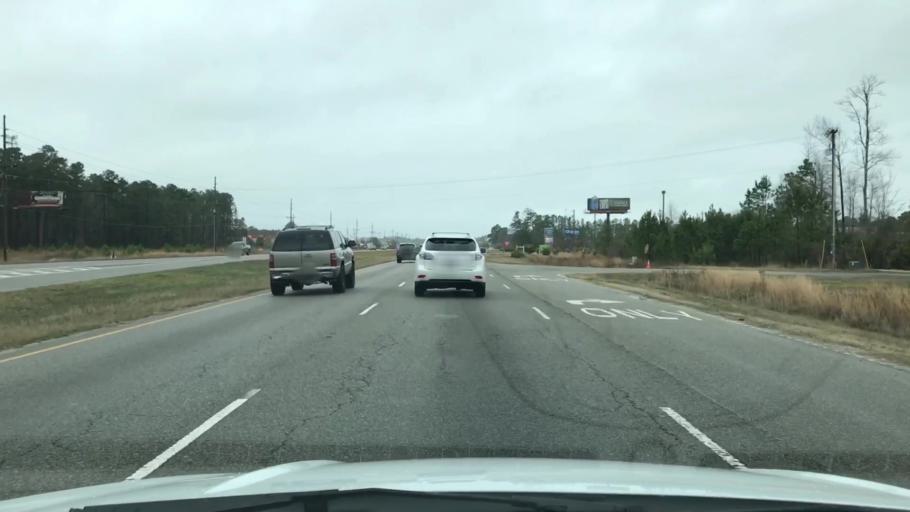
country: US
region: South Carolina
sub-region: Horry County
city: Red Hill
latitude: 33.7841
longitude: -78.9907
